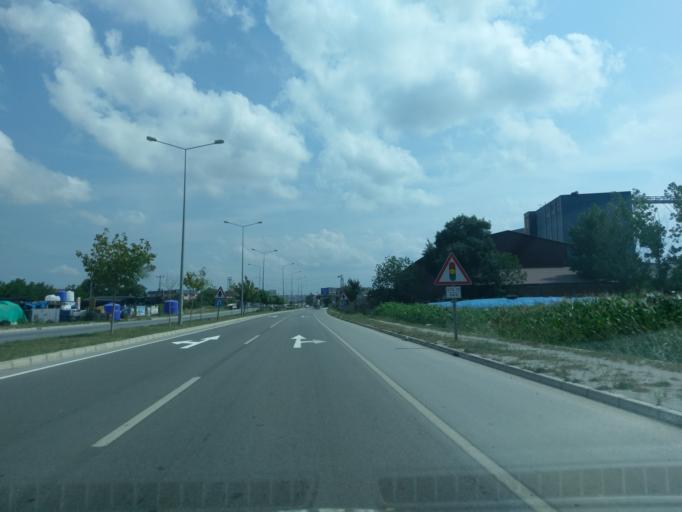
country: TR
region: Samsun
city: Bafra
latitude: 41.5713
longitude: 35.8721
